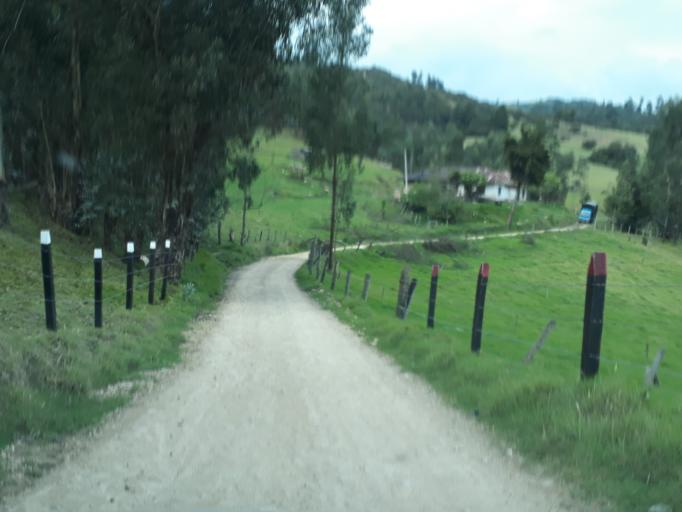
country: CO
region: Cundinamarca
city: Lenguazaque
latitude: 5.2640
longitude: -73.6960
